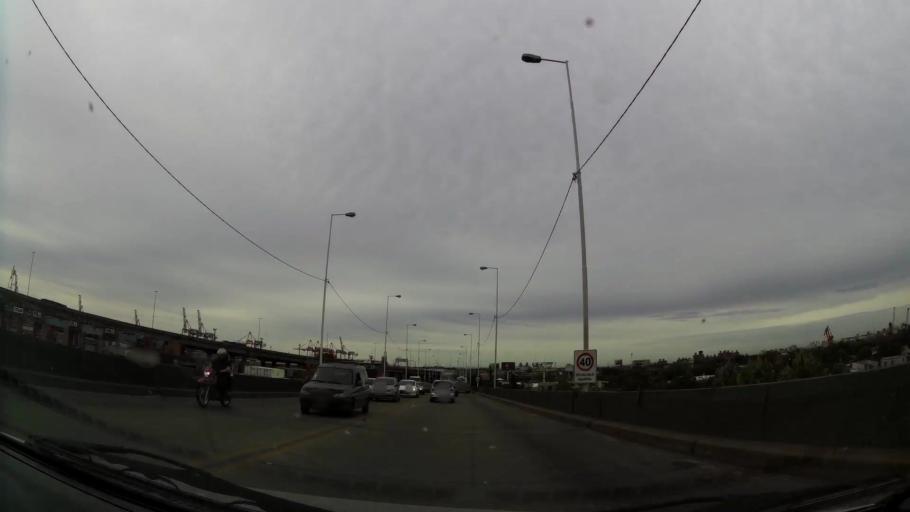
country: AR
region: Buenos Aires
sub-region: Partido de Avellaneda
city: Avellaneda
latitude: -34.6390
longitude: -58.3545
